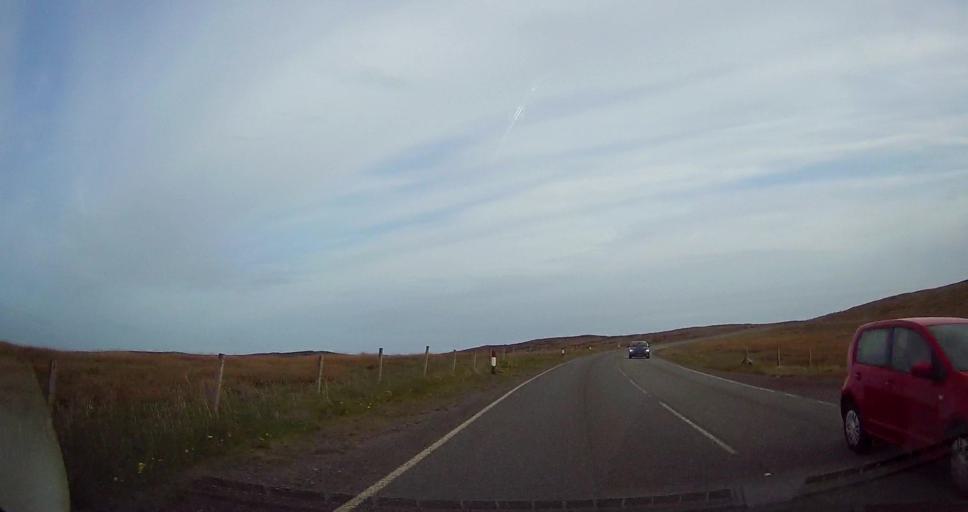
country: GB
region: Scotland
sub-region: Shetland Islands
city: Sandwick
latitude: 60.0939
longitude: -1.2303
